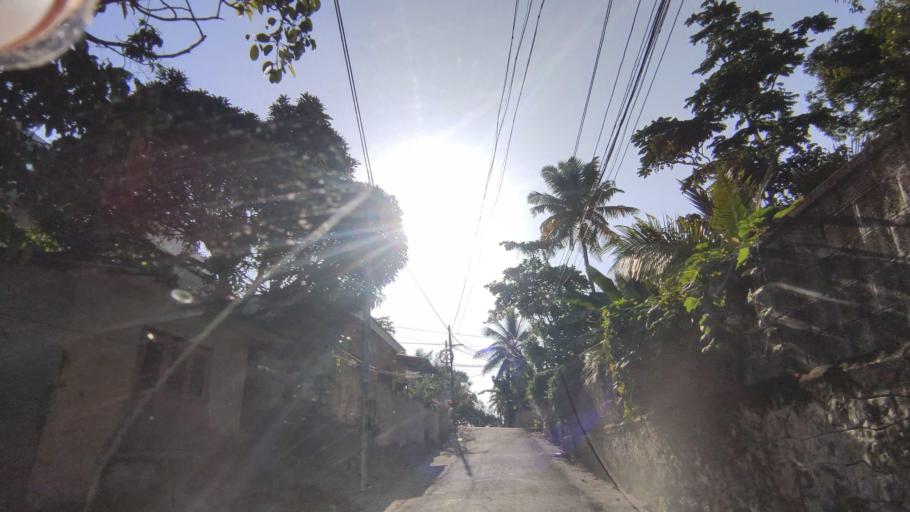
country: IN
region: Kerala
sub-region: Kottayam
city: Kottayam
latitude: 9.5929
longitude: 76.5108
